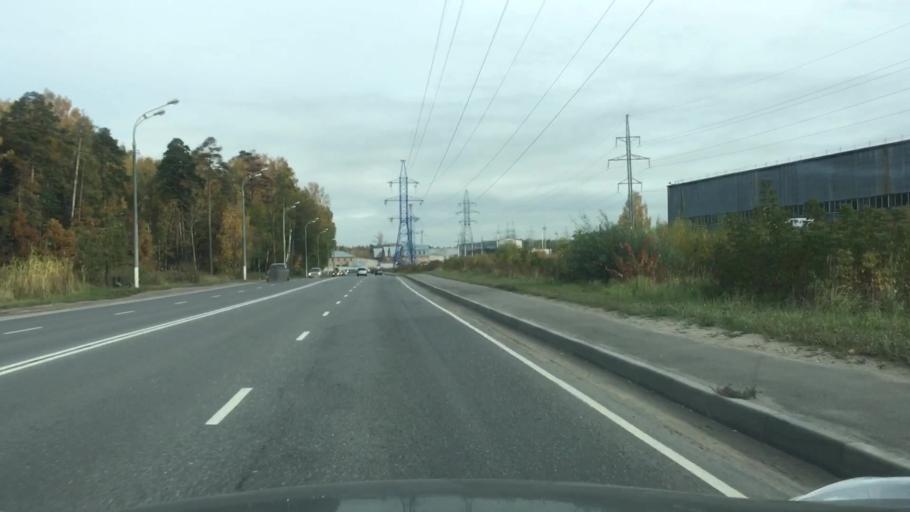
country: RU
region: Moscow
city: Vostochnyy
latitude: 55.7947
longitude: 37.8960
